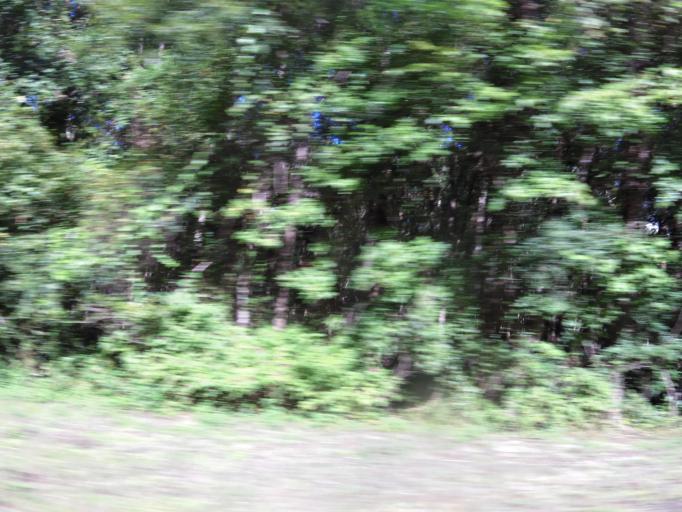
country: US
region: Georgia
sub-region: Camden County
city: Woodbine
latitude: 30.9964
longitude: -81.7307
